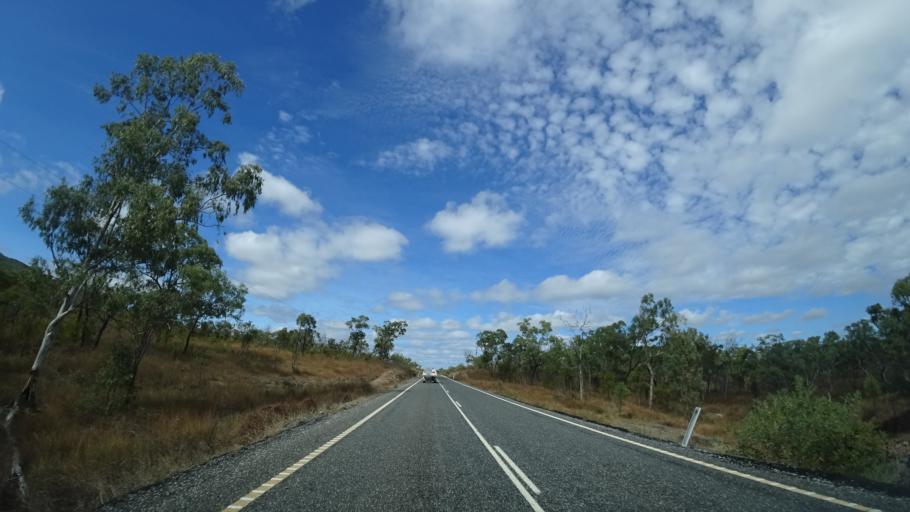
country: AU
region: Queensland
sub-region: Cairns
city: Port Douglas
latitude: -16.3710
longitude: 144.7339
